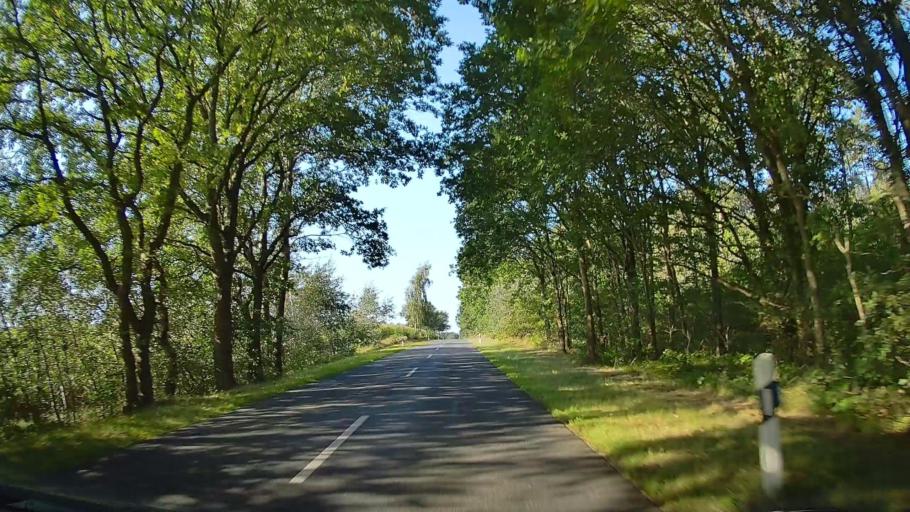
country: DE
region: Lower Saxony
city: Nordholz
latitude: 53.8070
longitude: 8.6021
